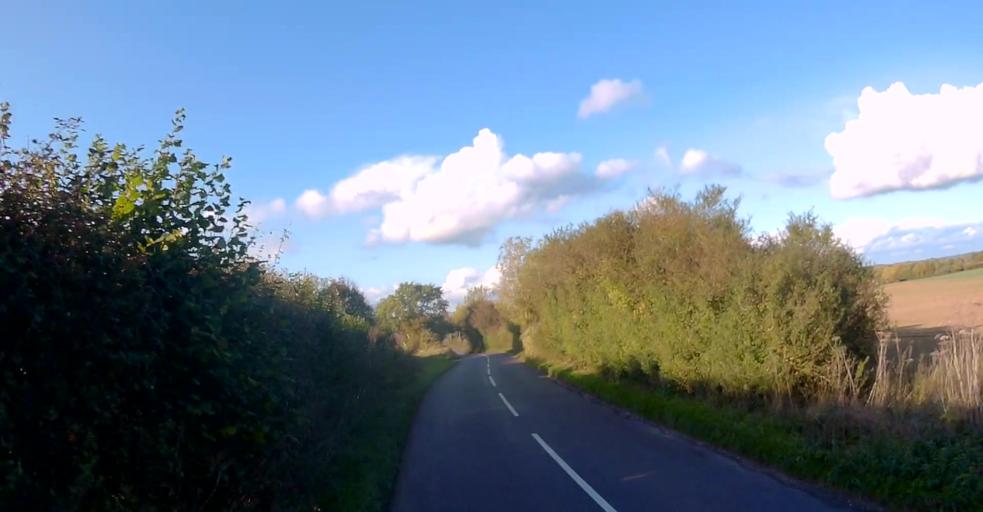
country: GB
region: England
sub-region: Hampshire
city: Odiham
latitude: 51.2428
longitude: -0.9315
